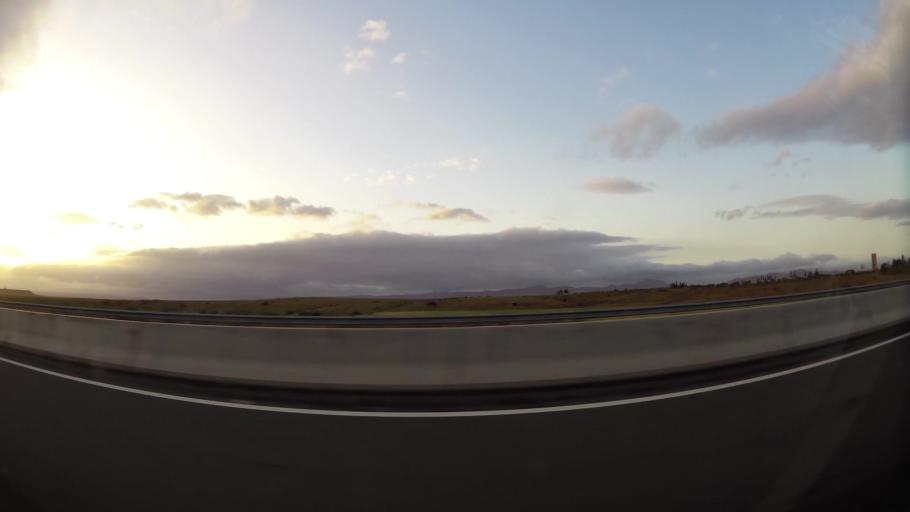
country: MA
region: Oriental
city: Taourirt
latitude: 34.5501
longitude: -2.8684
